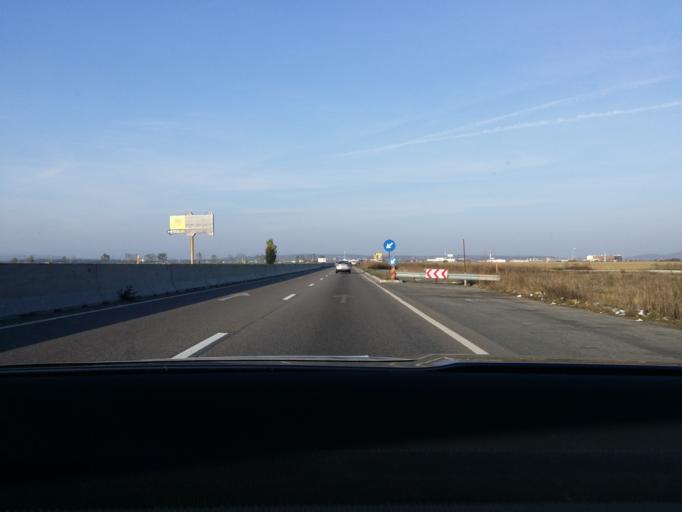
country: RO
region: Prahova
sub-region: Comuna Targsoru Vechi
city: Strejnicu
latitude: 44.9487
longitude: 25.9621
